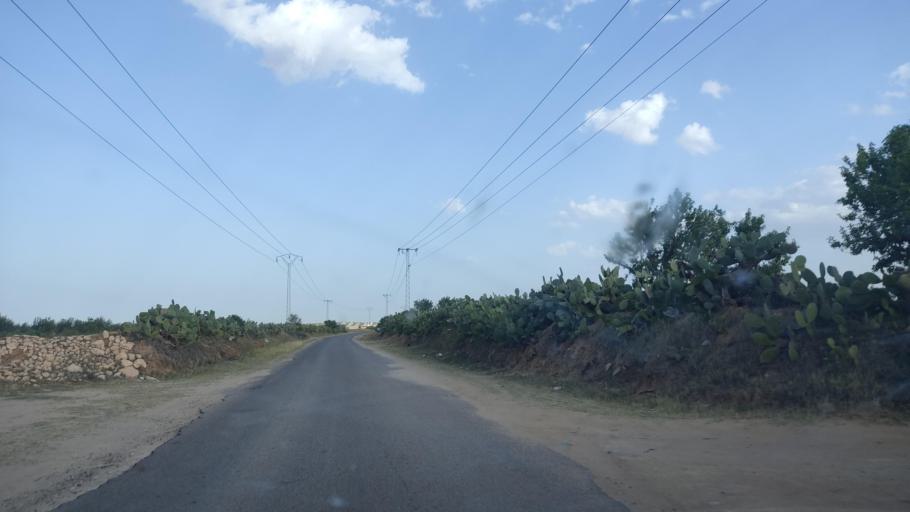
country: TN
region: Safaqis
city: Sfax
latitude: 34.8548
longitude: 10.6070
